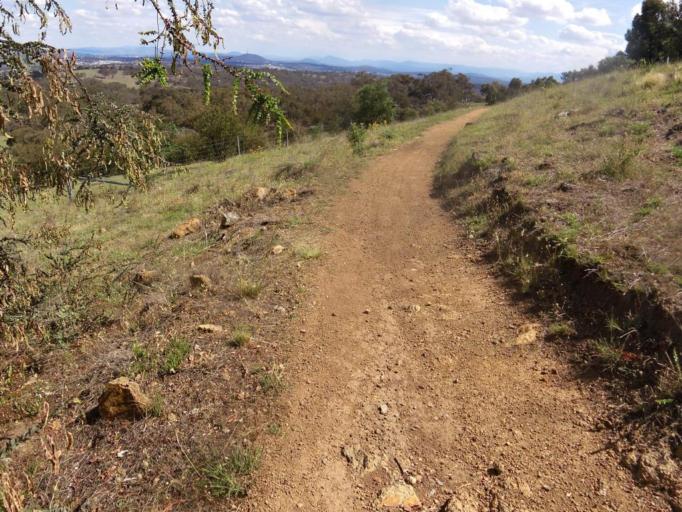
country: AU
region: Australian Capital Territory
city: Belconnen
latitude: -35.1522
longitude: 149.0868
